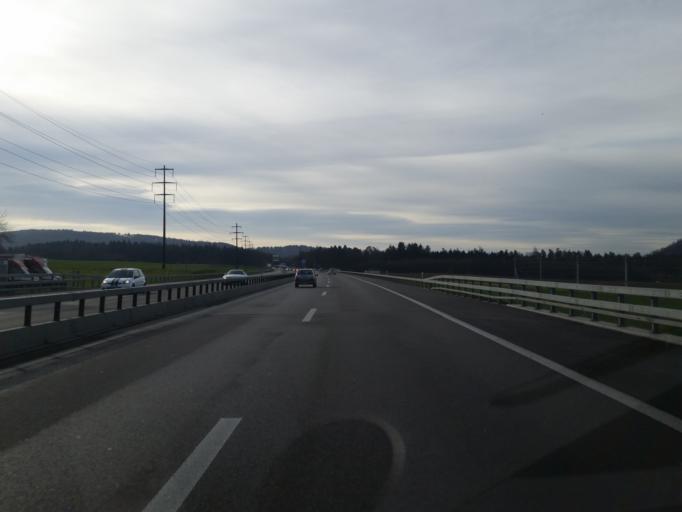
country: CH
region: Aargau
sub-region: Bezirk Baden
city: Birmenstorf
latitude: 47.4399
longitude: 8.2414
